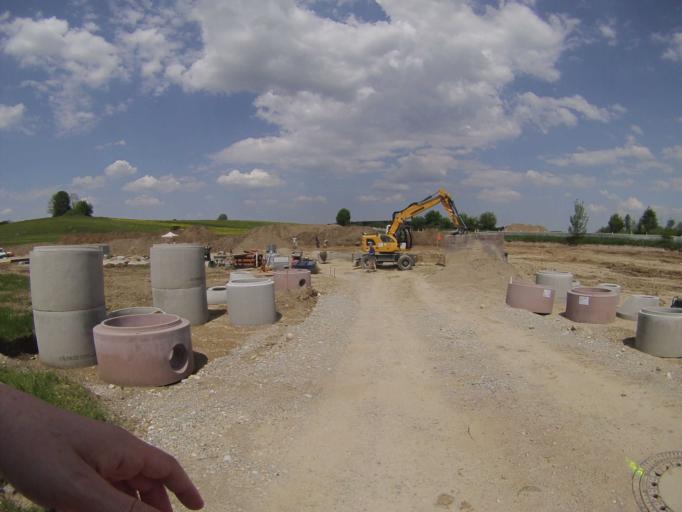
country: DE
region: Bavaria
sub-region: Upper Bavaria
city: Aying
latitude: 47.9467
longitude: 11.7907
